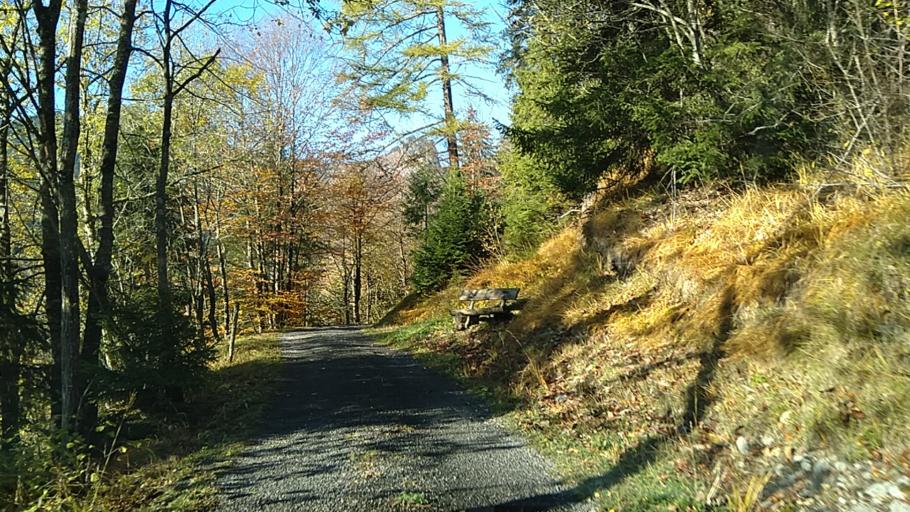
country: CH
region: Valais
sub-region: Monthey District
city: Vouvry
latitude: 46.3159
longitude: 6.8585
